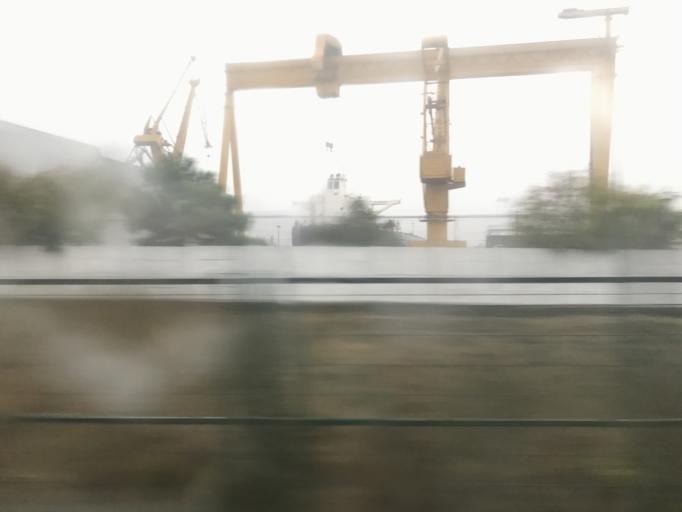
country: TR
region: Istanbul
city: Pendik
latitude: 40.8662
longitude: 29.2642
